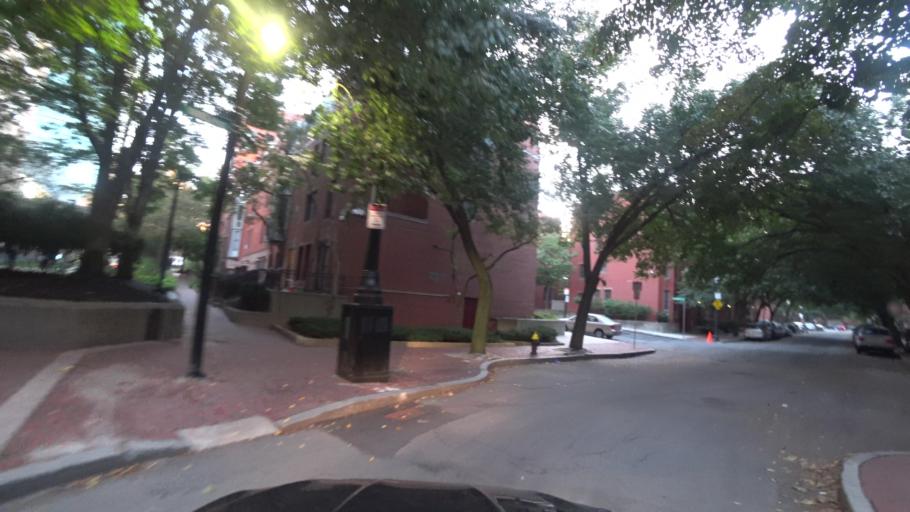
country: US
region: Massachusetts
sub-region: Suffolk County
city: Boston
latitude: 42.3463
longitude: -71.0776
